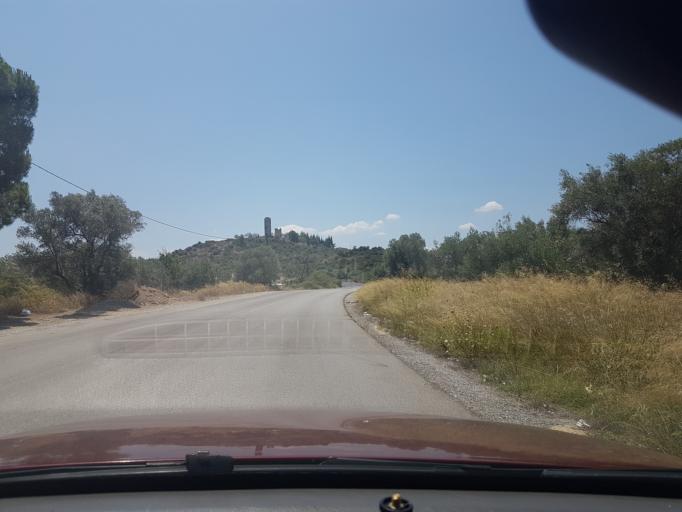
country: GR
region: Central Greece
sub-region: Nomos Evvoias
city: Filla
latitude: 38.4488
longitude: 23.6746
